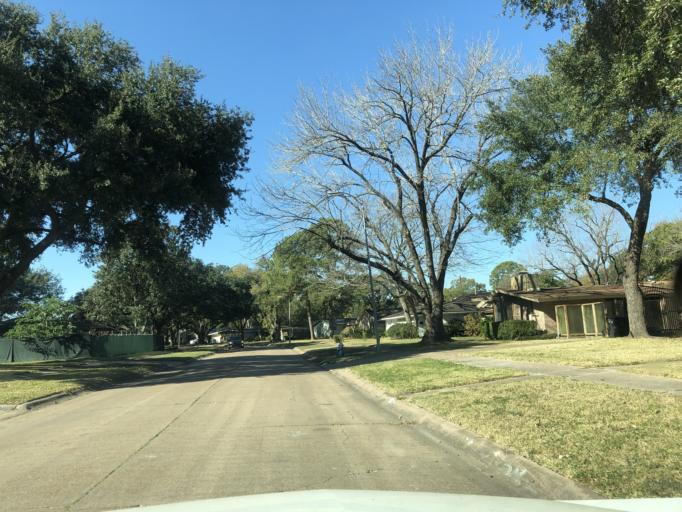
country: US
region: Texas
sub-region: Harris County
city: Bellaire
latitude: 29.6797
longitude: -95.4996
